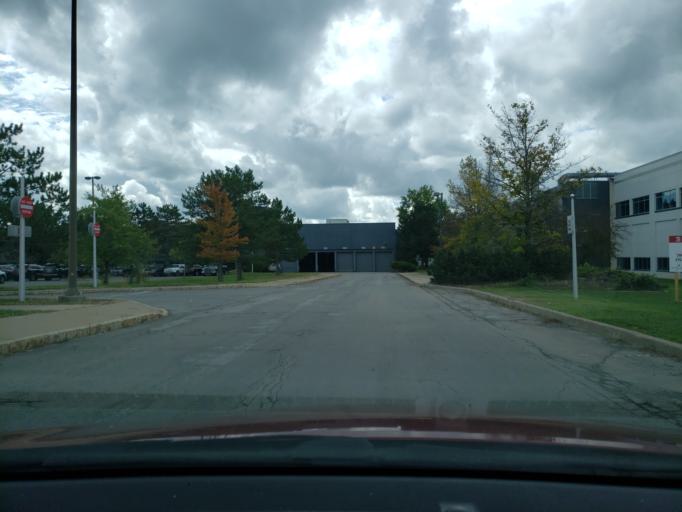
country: US
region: New York
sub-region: Monroe County
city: North Gates
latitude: 43.1544
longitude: -77.7464
